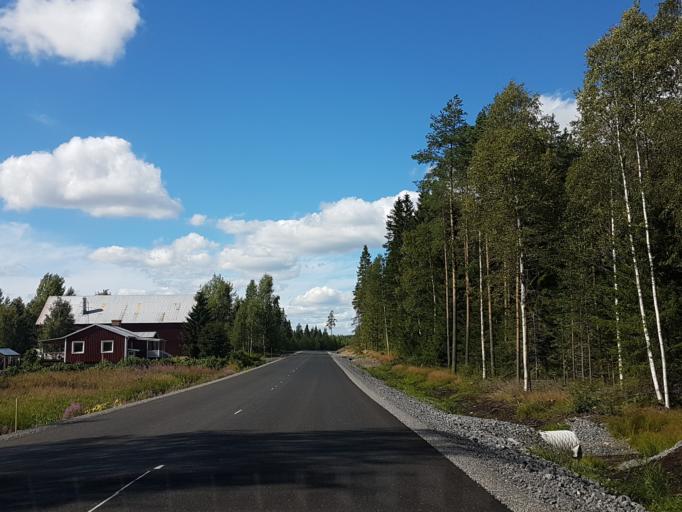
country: SE
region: Vaesterbotten
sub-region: Robertsfors Kommun
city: Robertsfors
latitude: 64.1314
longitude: 20.6399
